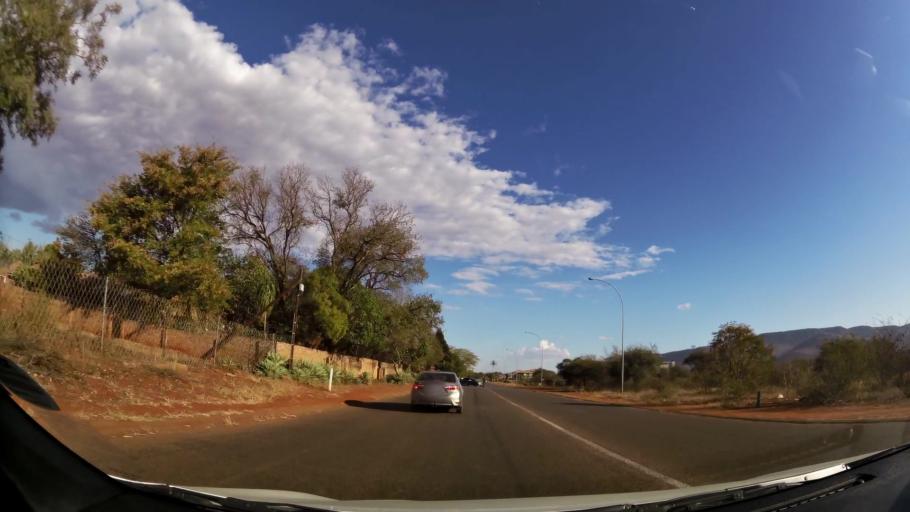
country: ZA
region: Limpopo
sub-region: Waterberg District Municipality
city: Mokopane
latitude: -24.1985
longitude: 29.0030
